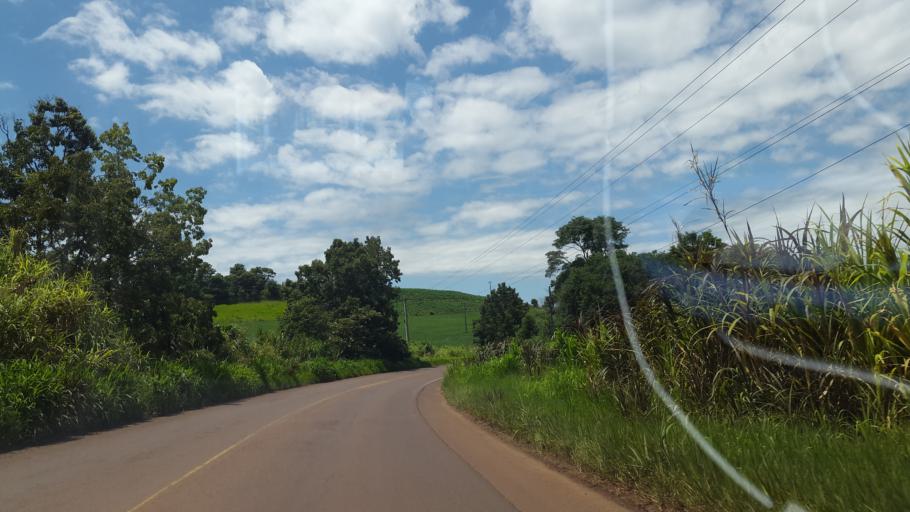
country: BR
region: Rio Grande do Sul
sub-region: Frederico Westphalen
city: Frederico Westphalen
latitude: -27.0485
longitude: -53.4806
